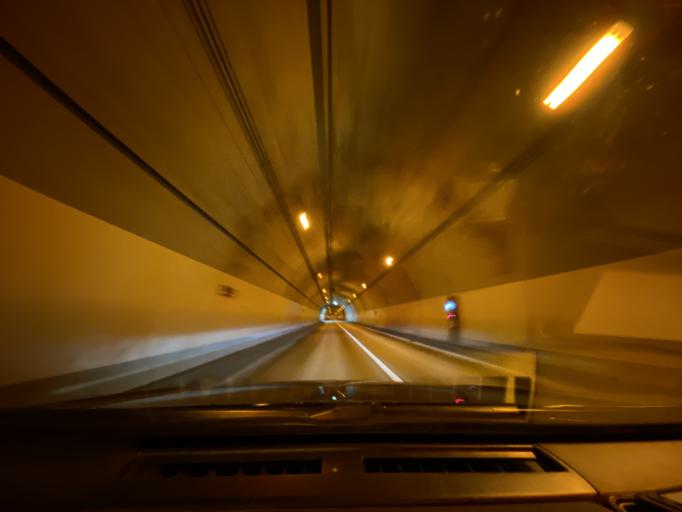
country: JP
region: Hokkaido
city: Rumoi
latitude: 43.8100
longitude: 141.4048
